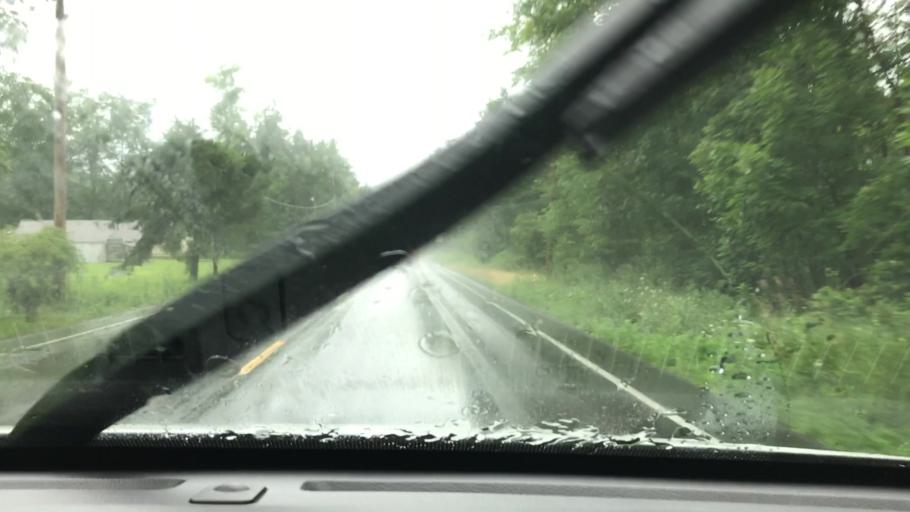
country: US
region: Pennsylvania
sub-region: Blair County
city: Tyrone
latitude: 40.7329
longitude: -78.1923
